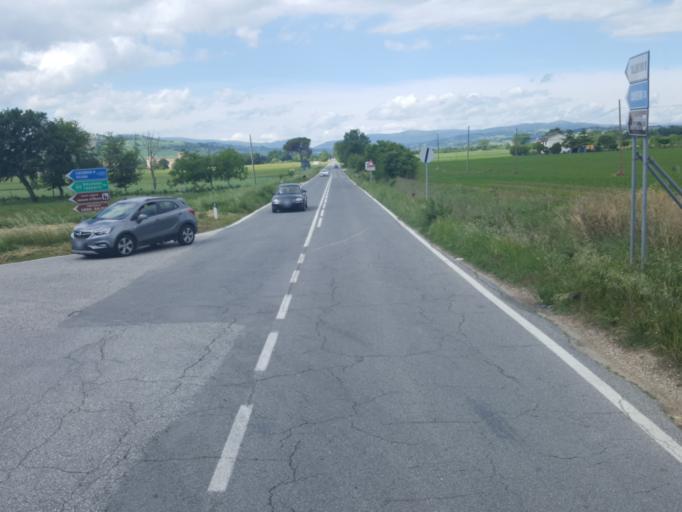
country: IT
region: The Marches
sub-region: Provincia di Macerata
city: Pollenza
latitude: 43.2386
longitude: 13.3656
